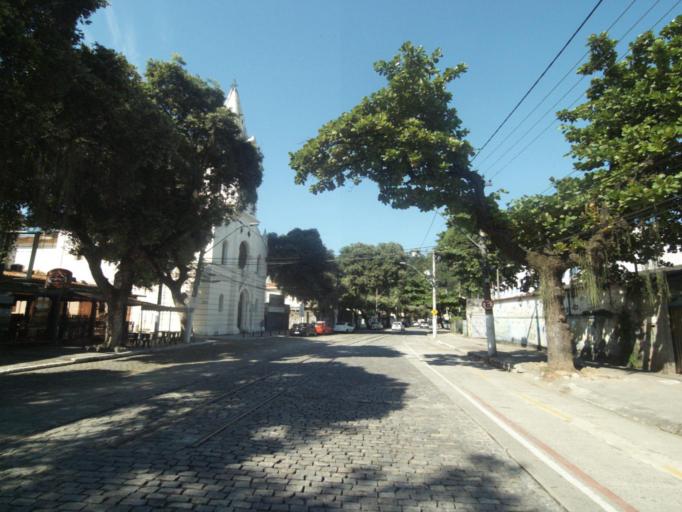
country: BR
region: Rio de Janeiro
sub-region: Niteroi
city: Niteroi
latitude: -22.8997
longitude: -43.1310
